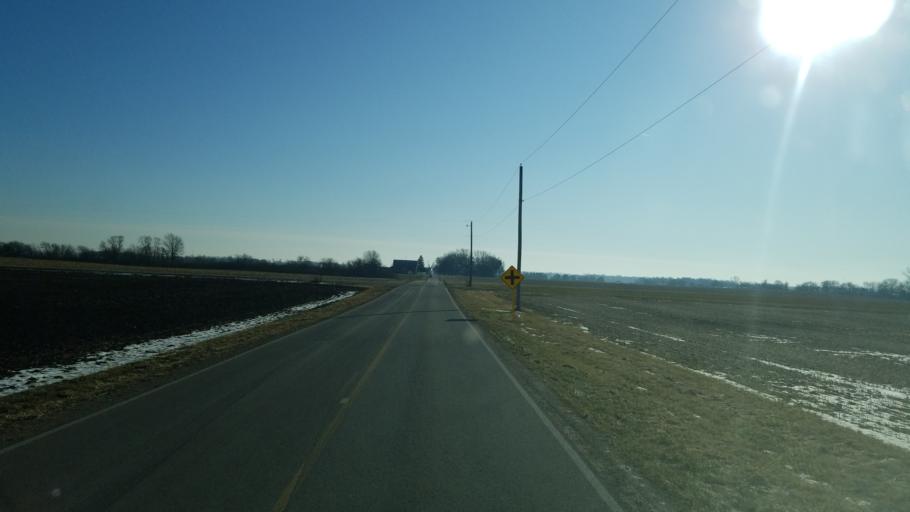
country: US
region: Ohio
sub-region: Huron County
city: Bellevue
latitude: 41.3153
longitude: -82.8785
